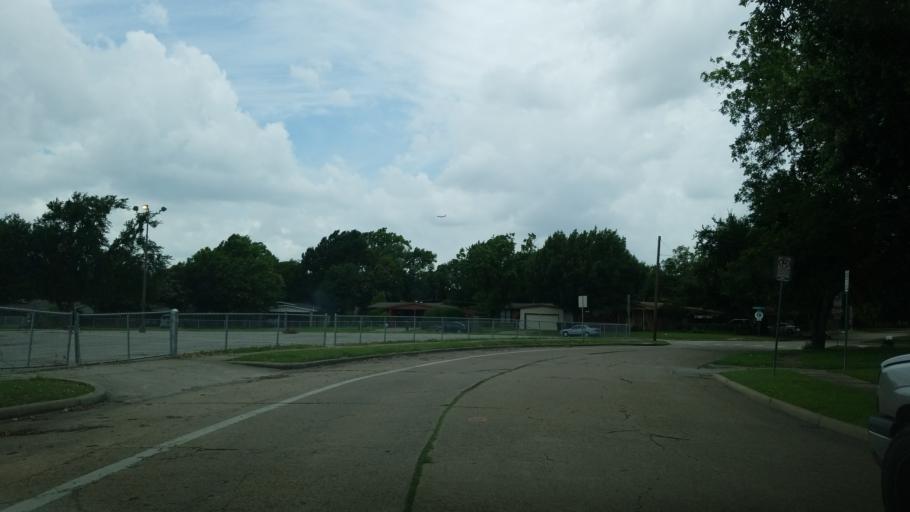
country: US
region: Texas
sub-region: Dallas County
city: Farmers Branch
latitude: 32.8896
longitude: -96.8749
